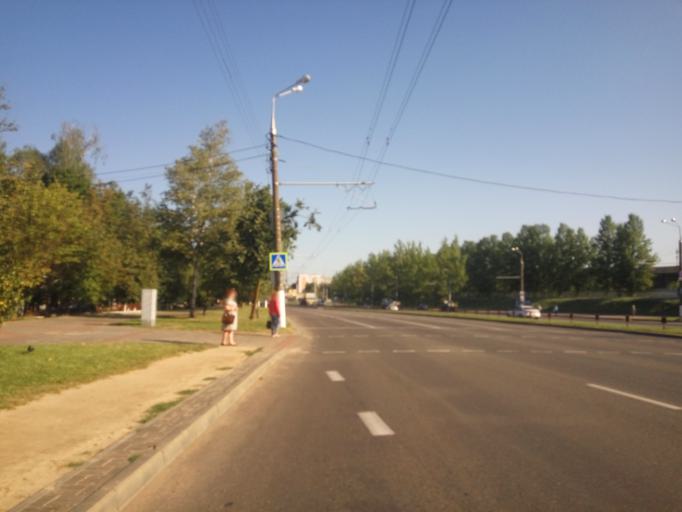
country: BY
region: Vitebsk
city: Vitebsk
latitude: 55.1927
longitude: 30.2499
